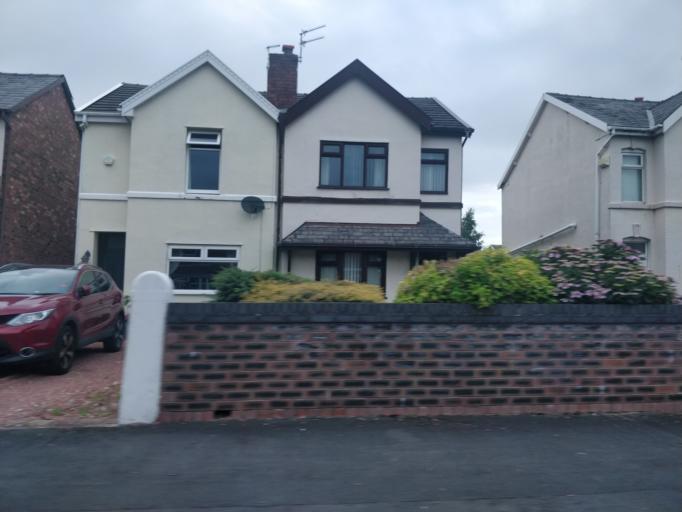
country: GB
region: England
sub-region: Sefton
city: Southport
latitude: 53.6498
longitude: -2.9700
